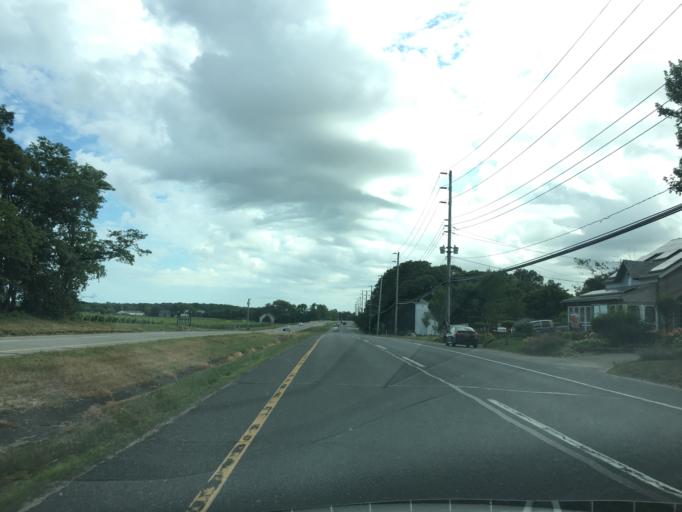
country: US
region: New York
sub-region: Suffolk County
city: Cutchogue
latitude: 41.0289
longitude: -72.4966
